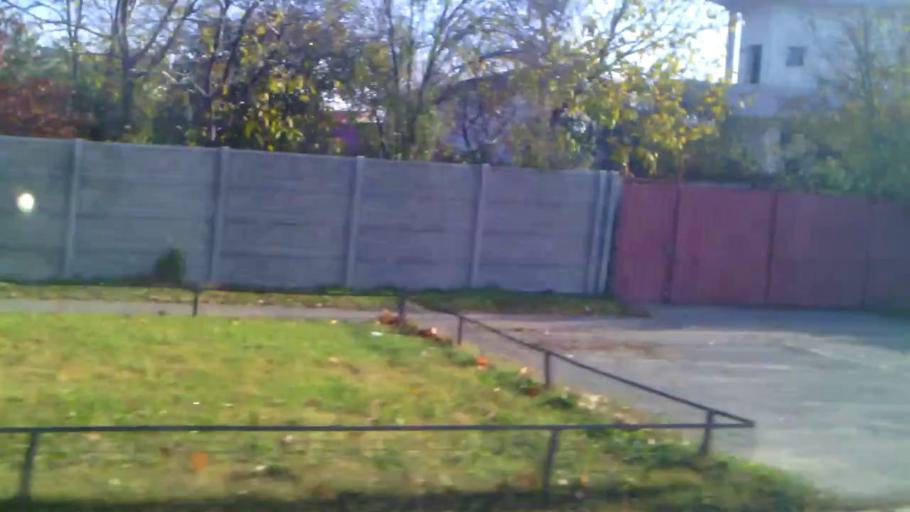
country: RO
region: Ilfov
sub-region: Comuna Popesti-Leordeni
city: Popesti-Leordeni
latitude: 44.3728
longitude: 26.1402
